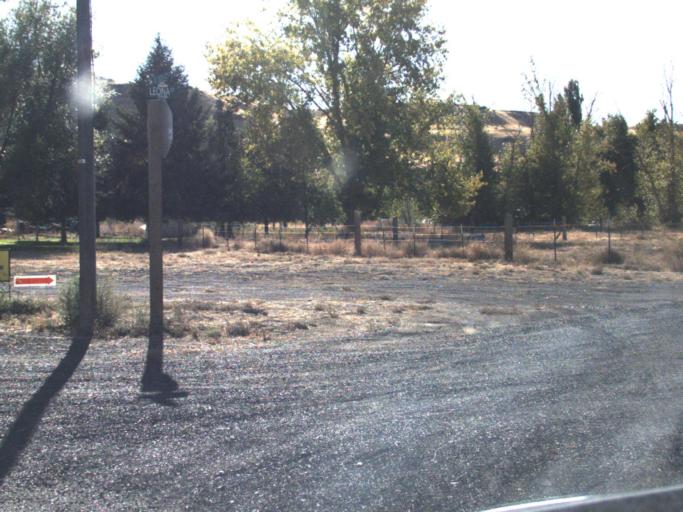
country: US
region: Washington
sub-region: Franklin County
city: Connell
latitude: 46.6446
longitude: -118.5580
